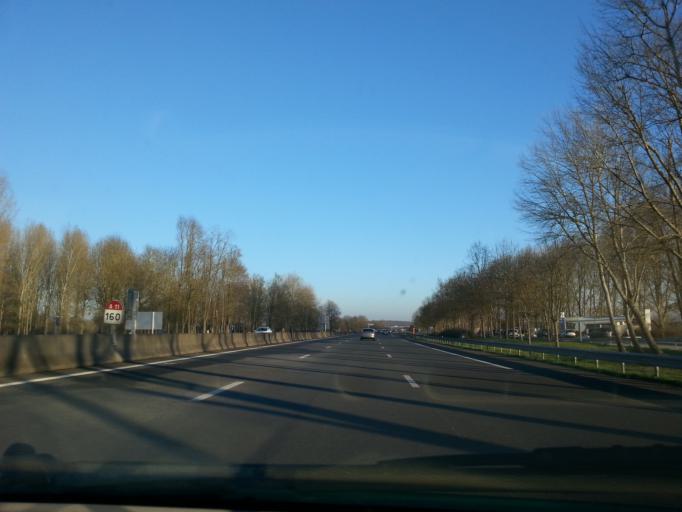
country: FR
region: Pays de la Loire
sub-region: Departement de la Sarthe
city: Champagne
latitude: 48.0532
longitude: 0.3277
